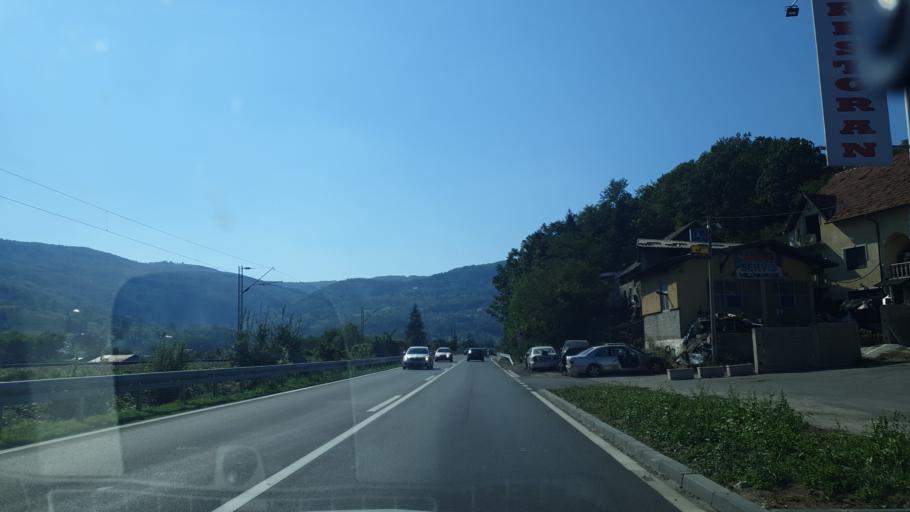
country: RS
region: Central Serbia
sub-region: Zlatiborski Okrug
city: Pozega
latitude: 43.8066
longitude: 19.9569
